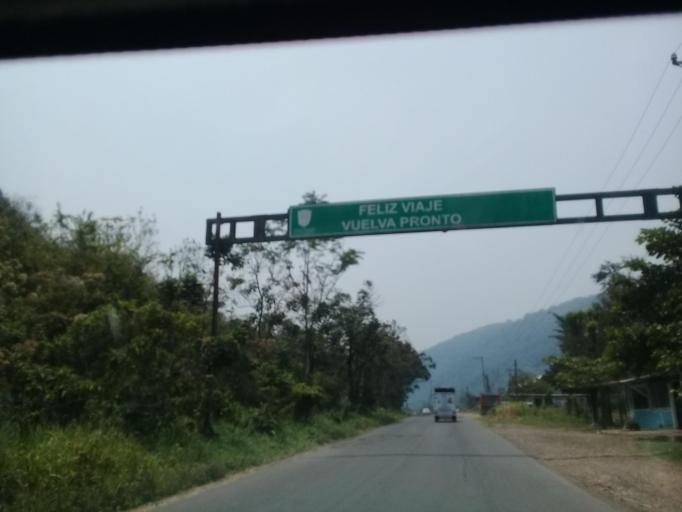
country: MX
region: Veracruz
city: Tezonapa
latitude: 18.6119
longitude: -96.6939
